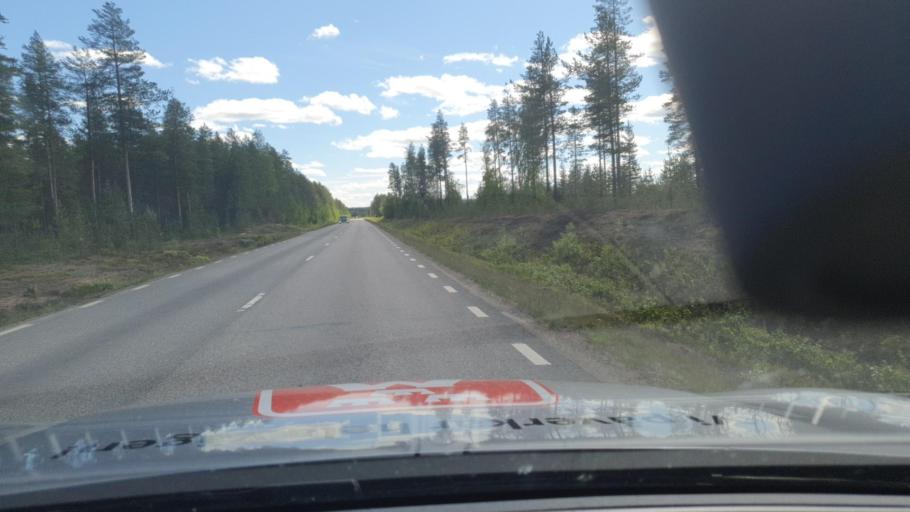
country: SE
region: Norrbotten
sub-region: Pajala Kommun
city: Pajala
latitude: 67.2489
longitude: 23.0755
